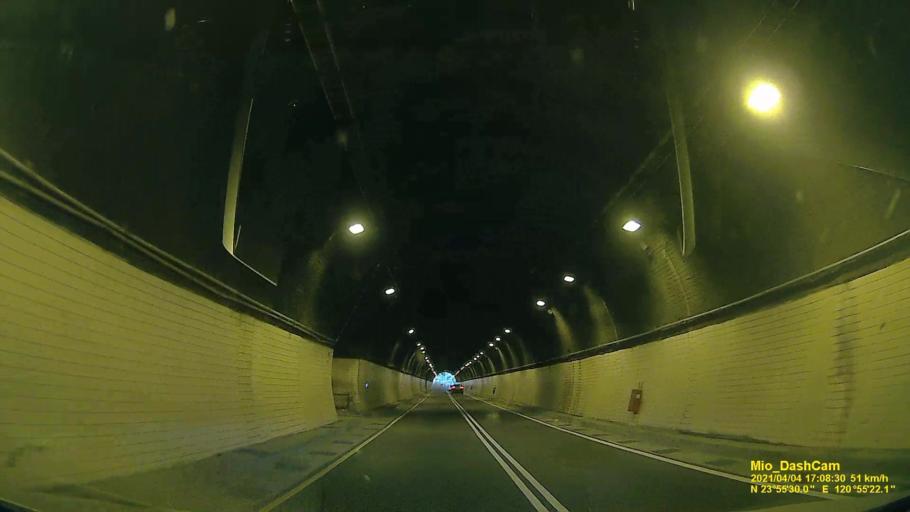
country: TW
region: Taiwan
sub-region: Nantou
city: Puli
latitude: 23.9251
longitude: 120.9228
